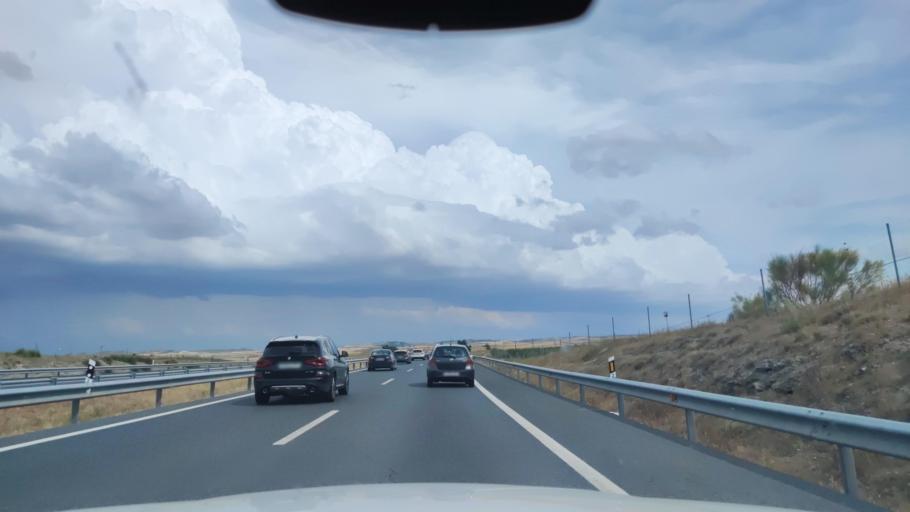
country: ES
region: Madrid
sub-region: Provincia de Madrid
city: Fuentiduena de Tajo
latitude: 40.0967
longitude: -3.1238
